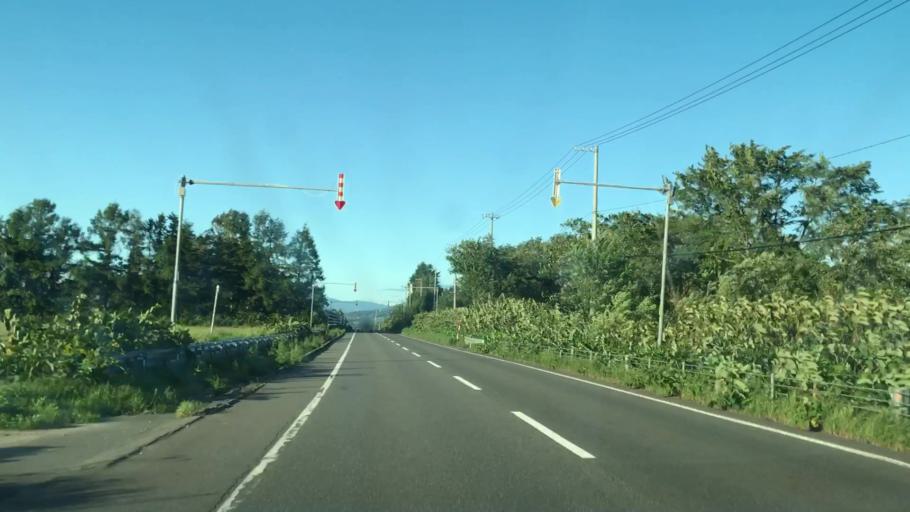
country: JP
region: Hokkaido
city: Date
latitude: 42.6186
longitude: 140.7916
